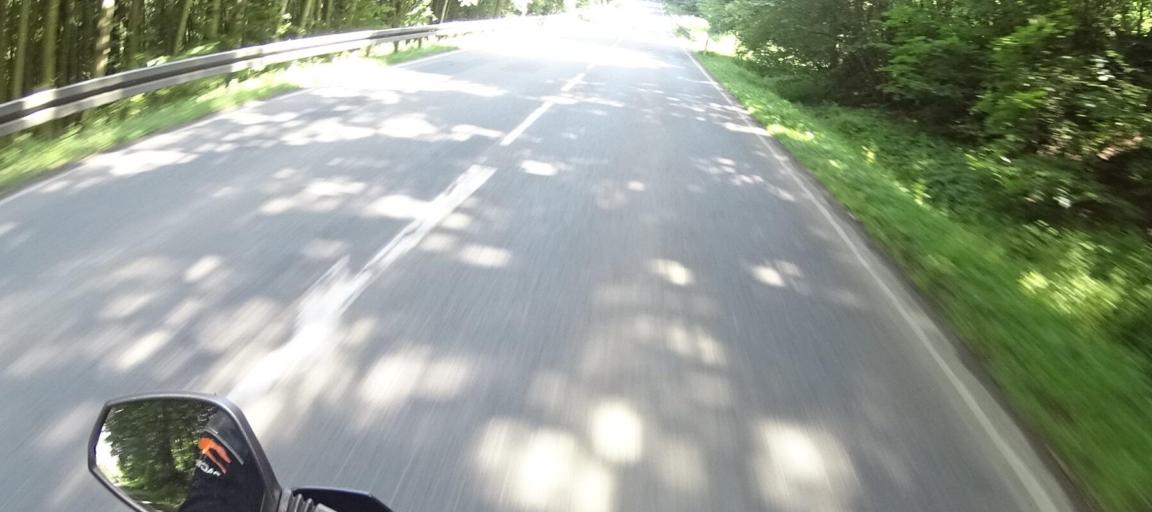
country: DE
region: Lower Saxony
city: Holzminden
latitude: 51.7854
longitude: 9.4350
